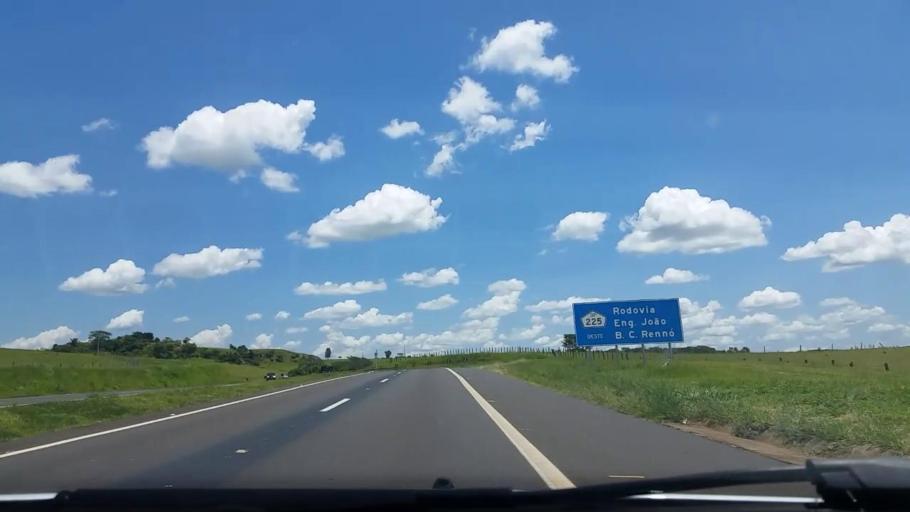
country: BR
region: Sao Paulo
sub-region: Bauru
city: Bauru
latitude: -22.4269
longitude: -49.1298
